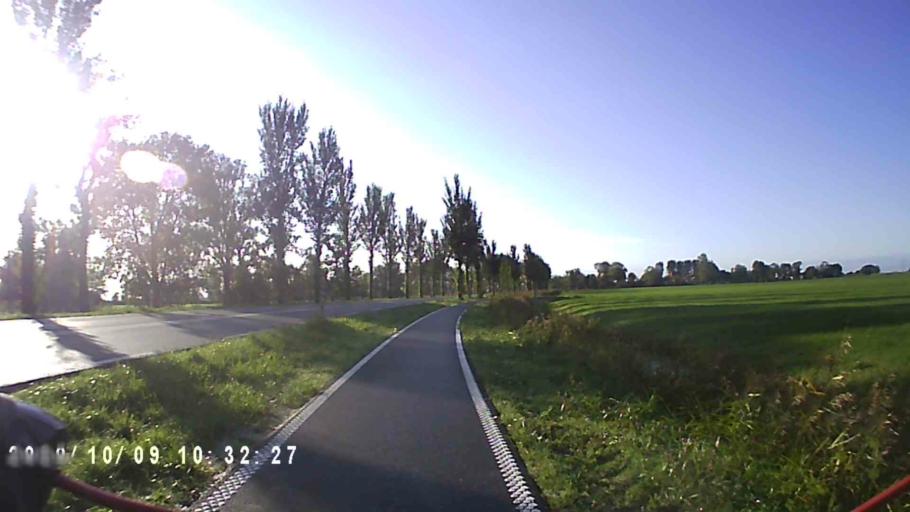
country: NL
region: Groningen
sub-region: Gemeente Winsum
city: Winsum
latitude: 53.3086
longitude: 6.5323
